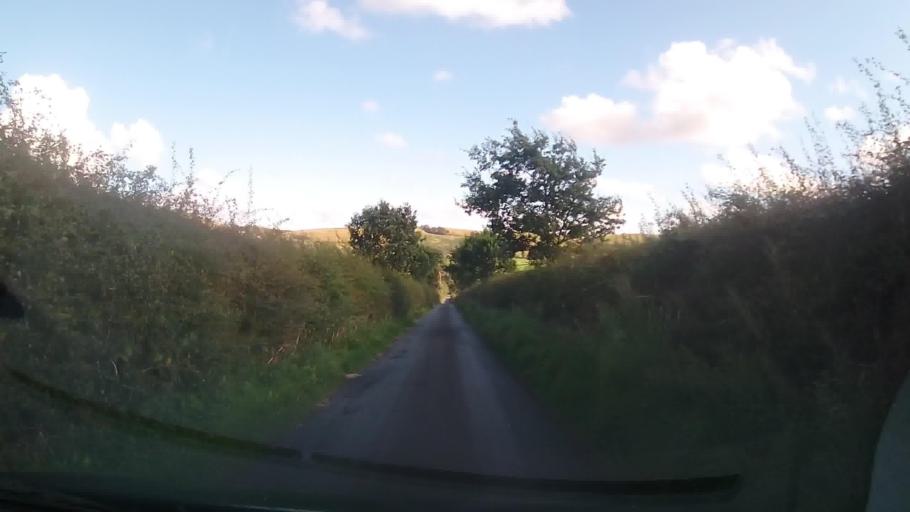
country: GB
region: England
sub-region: Shropshire
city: Norbury
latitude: 52.5649
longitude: -2.9003
